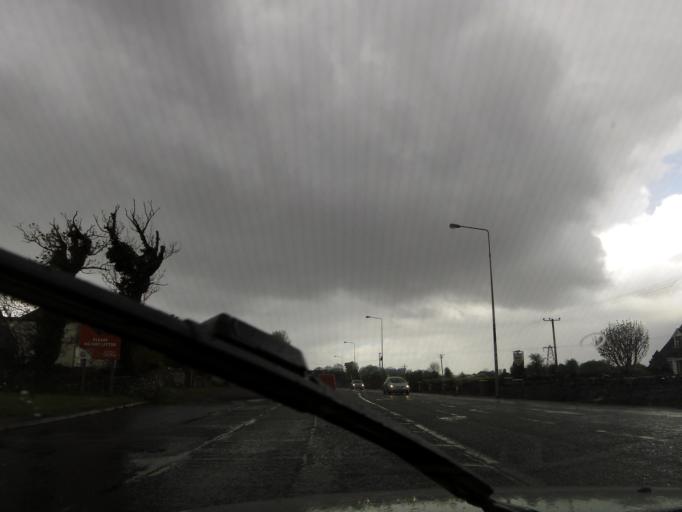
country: IE
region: Connaught
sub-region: County Galway
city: Gaillimh
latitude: 53.2977
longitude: -9.0118
